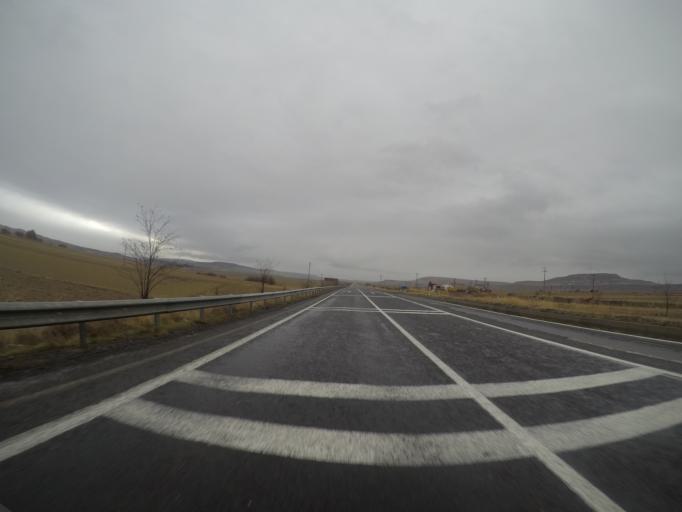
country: TR
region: Nevsehir
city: Urgub
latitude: 38.7177
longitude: 34.9401
